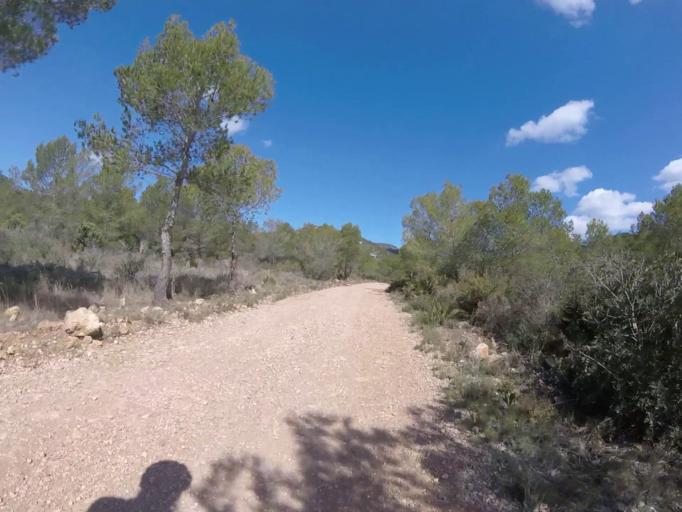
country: ES
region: Valencia
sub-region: Provincia de Castello
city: Alcoceber
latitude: 40.2904
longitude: 0.3166
